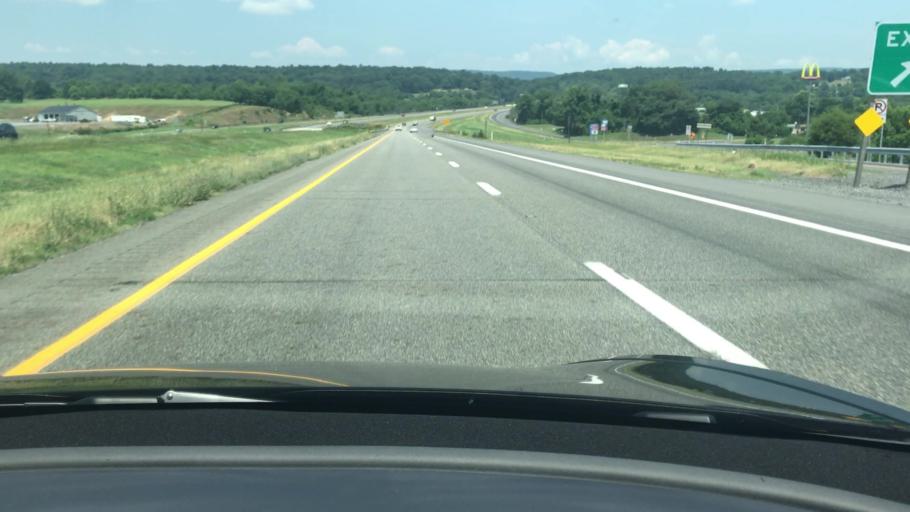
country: US
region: Pennsylvania
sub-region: Juniata County
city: Mifflintown
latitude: 40.5782
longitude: -77.3706
